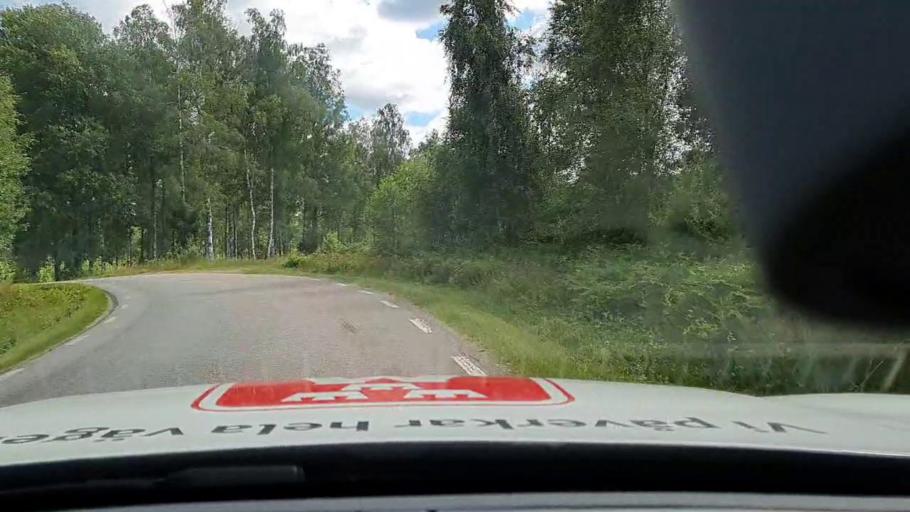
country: SE
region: Vaestra Goetaland
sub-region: Karlsborgs Kommun
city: Molltorp
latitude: 58.6047
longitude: 14.3026
